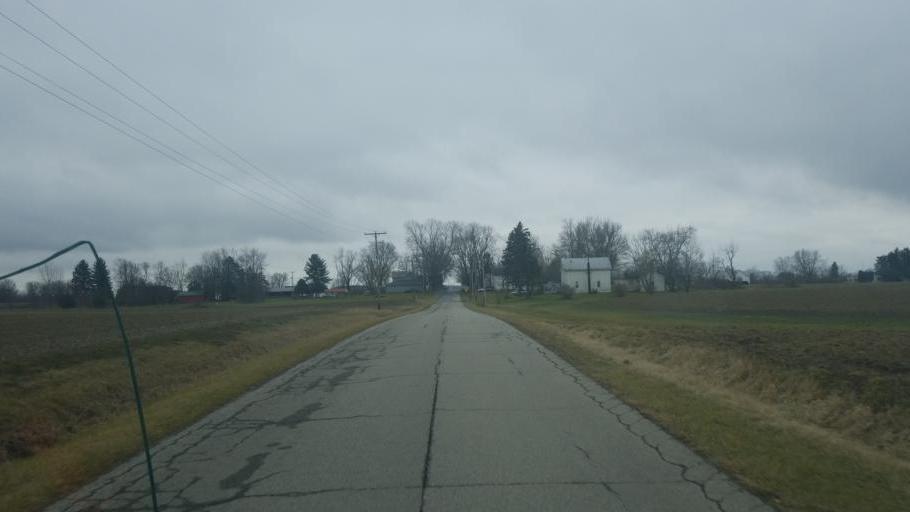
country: US
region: Ohio
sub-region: Crawford County
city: Bucyrus
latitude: 40.7223
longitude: -82.9185
